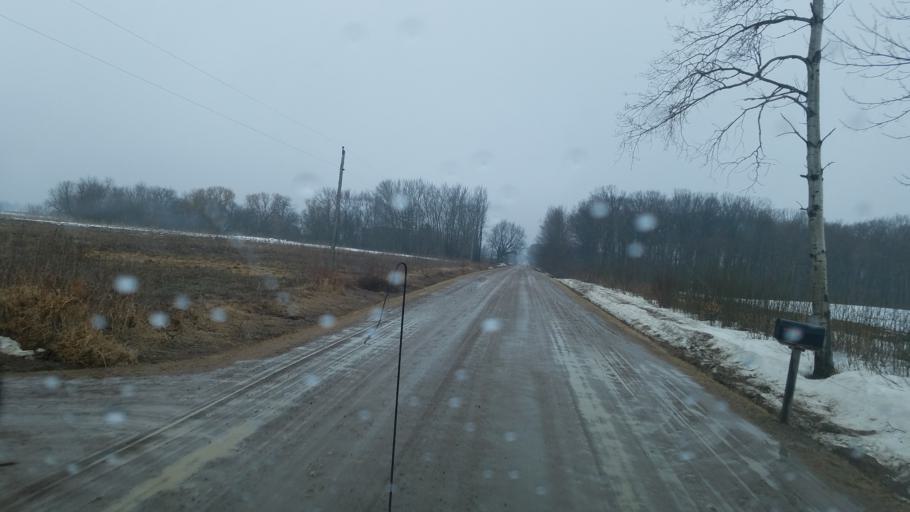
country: US
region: Wisconsin
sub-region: Clark County
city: Loyal
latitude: 44.6371
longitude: -90.3973
